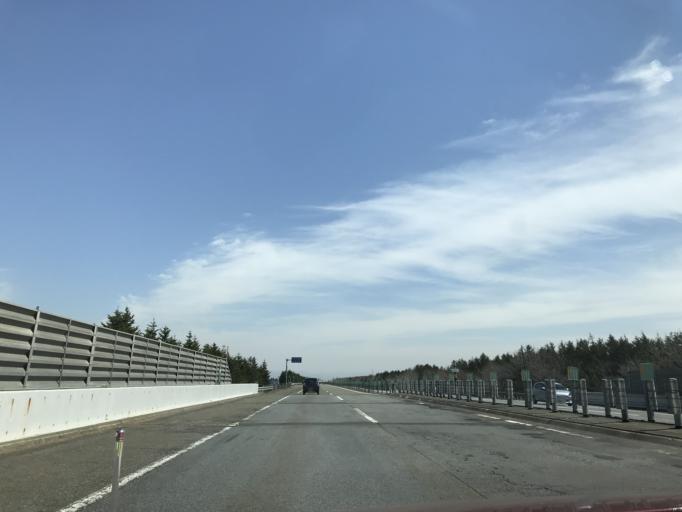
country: JP
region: Hokkaido
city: Ebetsu
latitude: 43.1251
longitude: 141.6388
